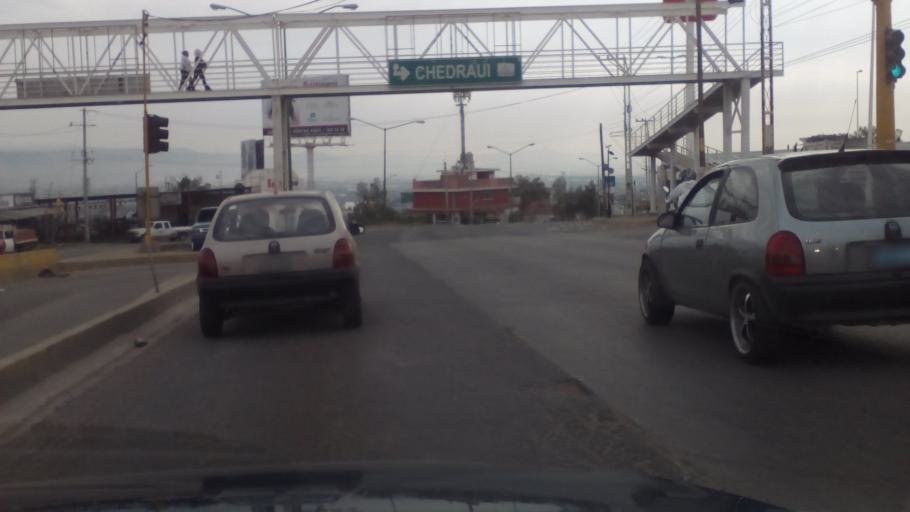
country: MX
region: Guanajuato
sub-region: Leon
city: La Ermita
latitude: 21.1353
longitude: -101.7184
